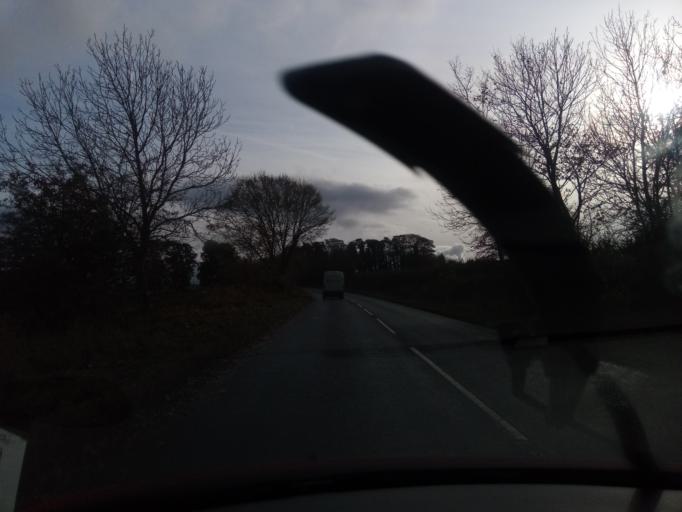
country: GB
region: England
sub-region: Northumberland
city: Birtley
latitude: 55.0470
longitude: -2.1544
